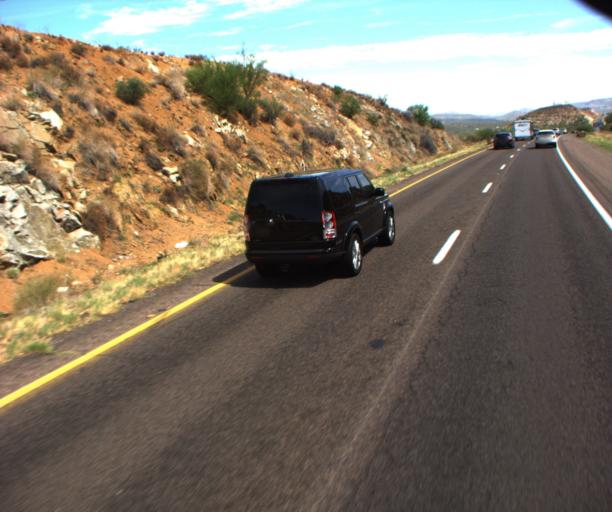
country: US
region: Arizona
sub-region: Yavapai County
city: Black Canyon City
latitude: 34.0264
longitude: -112.1454
